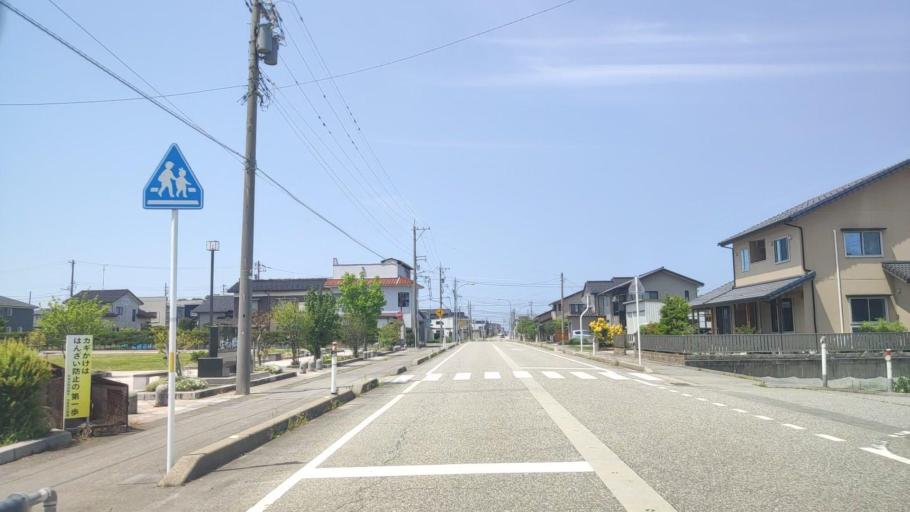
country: JP
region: Toyama
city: Nyuzen
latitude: 36.9538
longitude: 137.5646
